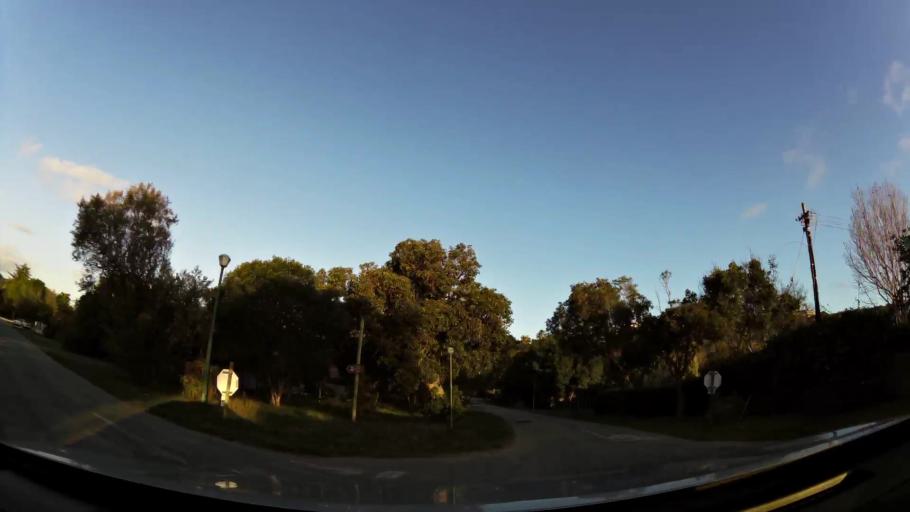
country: ZA
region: Western Cape
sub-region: Eden District Municipality
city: Knysna
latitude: -34.0200
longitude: 22.8049
